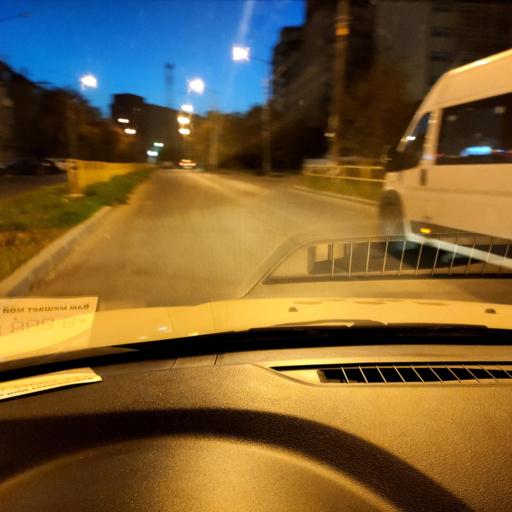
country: RU
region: Samara
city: Tol'yatti
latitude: 53.5221
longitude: 49.4151
